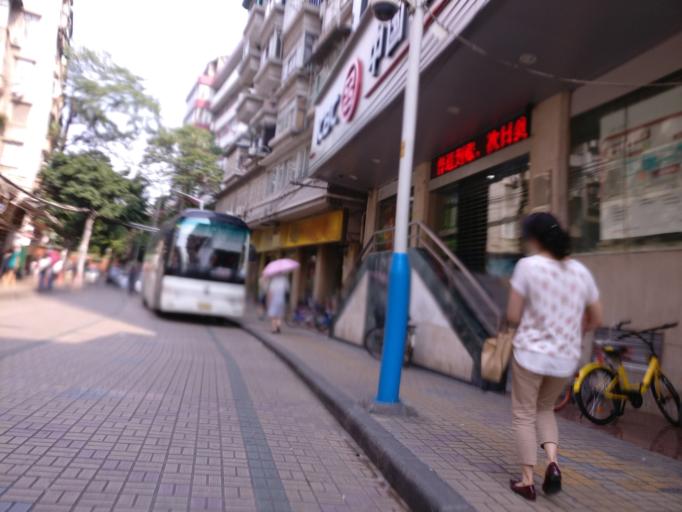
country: CN
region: Guangdong
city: Guangzhou
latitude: 23.1241
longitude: 113.2902
